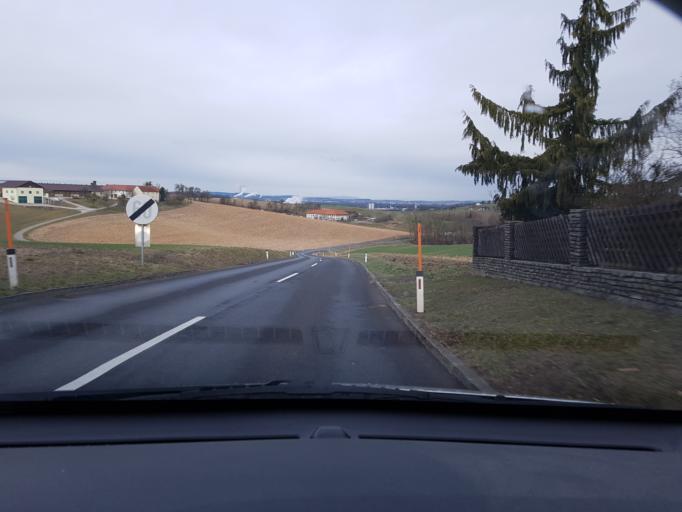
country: AT
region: Upper Austria
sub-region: Politischer Bezirk Linz-Land
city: Ansfelden
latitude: 48.1745
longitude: 14.2787
